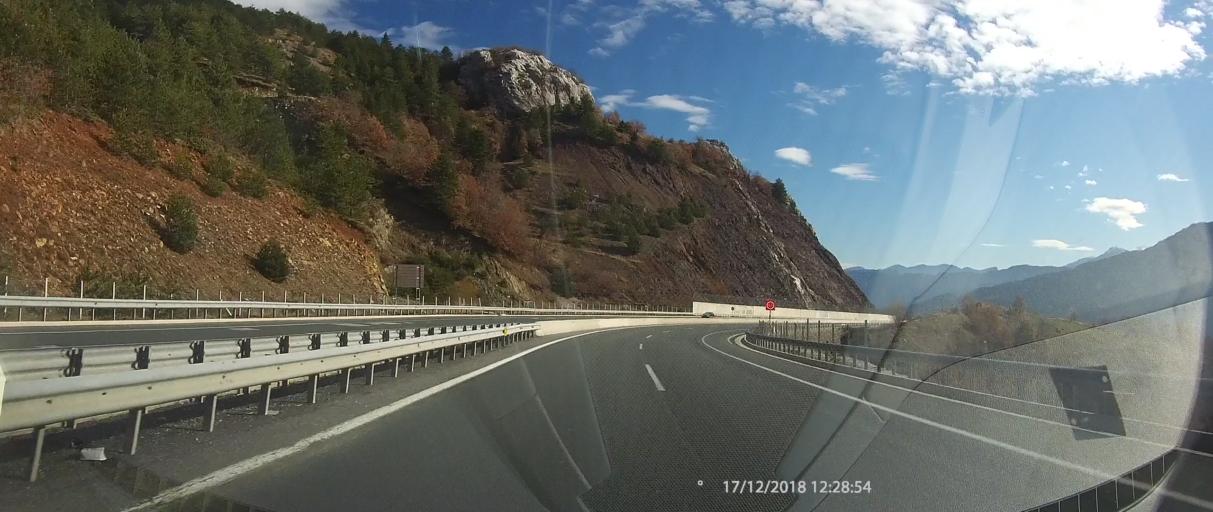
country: GR
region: Epirus
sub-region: Nomos Ioanninon
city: Metsovo
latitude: 39.7868
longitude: 21.2828
